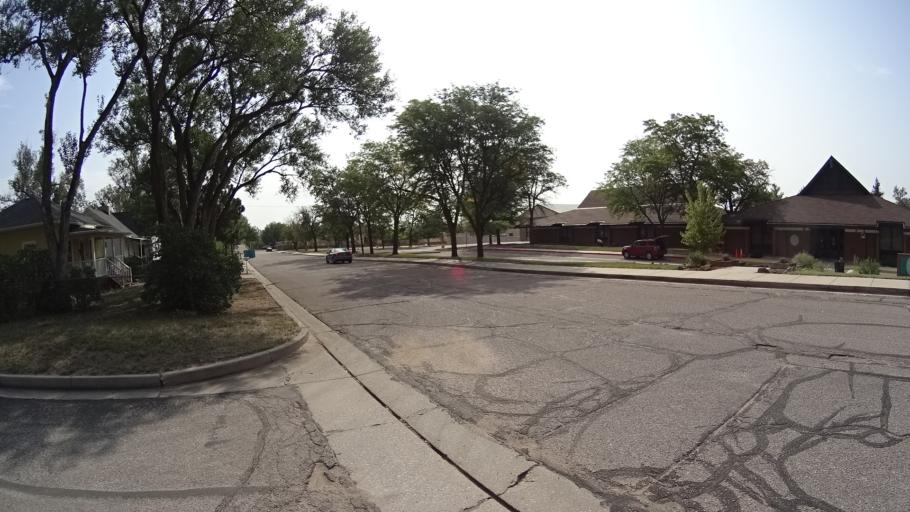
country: US
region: Colorado
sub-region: El Paso County
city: Colorado Springs
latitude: 38.8471
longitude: -104.7845
